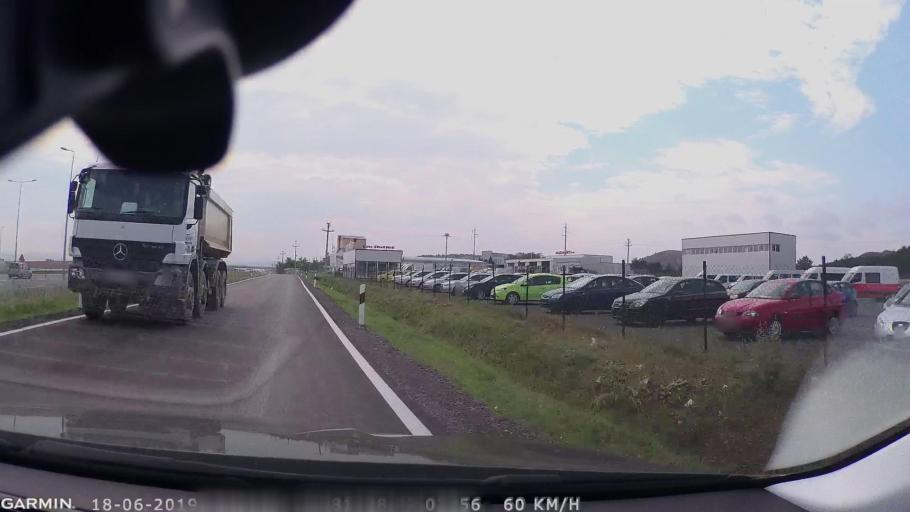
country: MK
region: Sveti Nikole
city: Sveti Nikole
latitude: 41.8032
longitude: 22.0136
